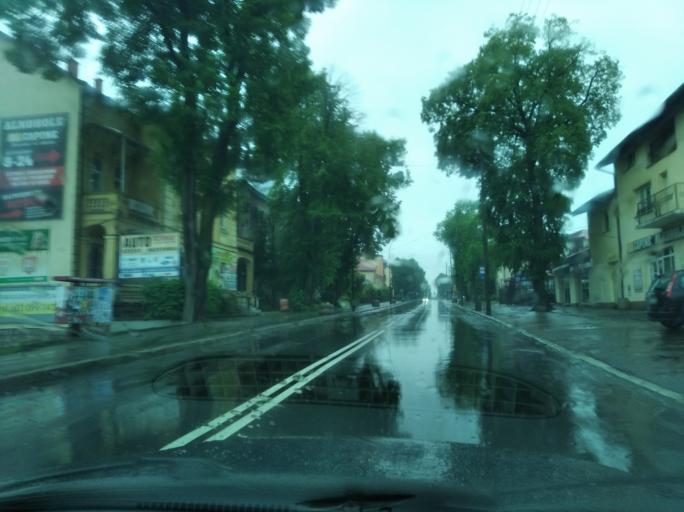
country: PL
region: Subcarpathian Voivodeship
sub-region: Powiat jasielski
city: Jaslo
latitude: 49.7417
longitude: 21.4684
